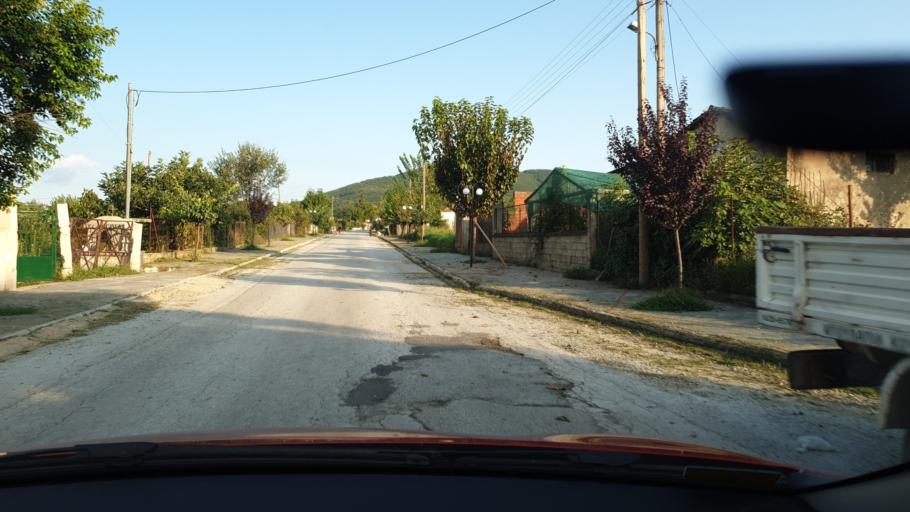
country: GR
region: Central Macedonia
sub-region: Nomos Chalkidikis
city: Galatista
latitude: 40.5579
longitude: 23.2988
